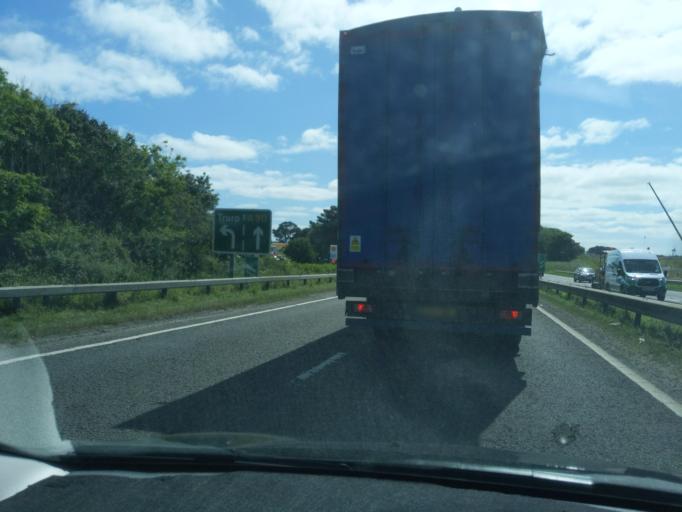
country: GB
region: England
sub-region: Cornwall
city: Newquay
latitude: 50.3486
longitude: -5.0255
